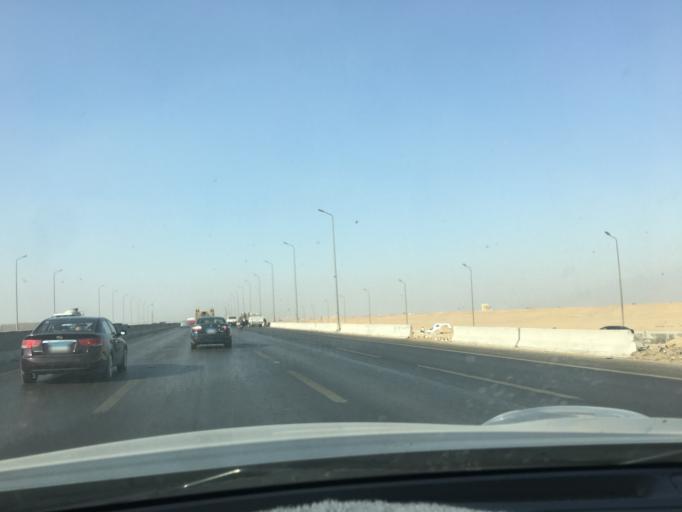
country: EG
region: Muhafazat al Qalyubiyah
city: Al Khankah
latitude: 30.1132
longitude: 31.4570
